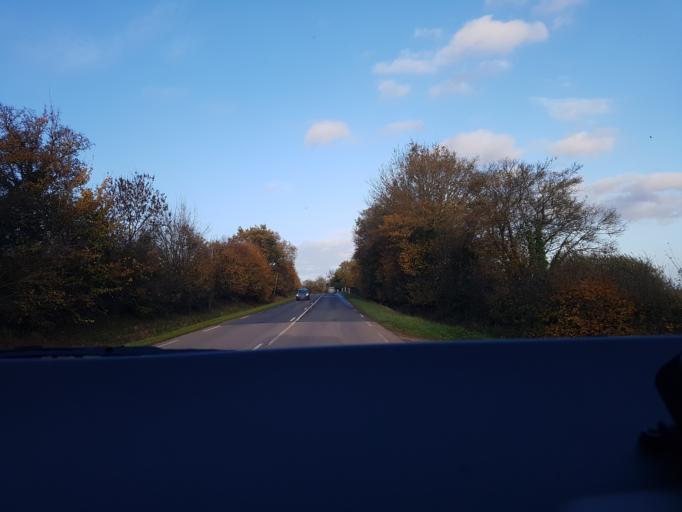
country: FR
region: Lower Normandy
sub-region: Departement du Calvados
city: Troarn
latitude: 49.1944
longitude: -0.1391
